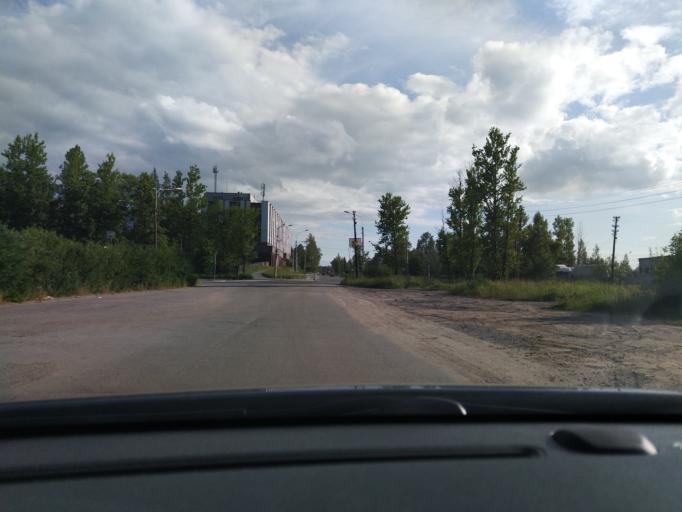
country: RU
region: St.-Petersburg
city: Gorelovo
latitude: 59.7814
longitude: 30.1505
